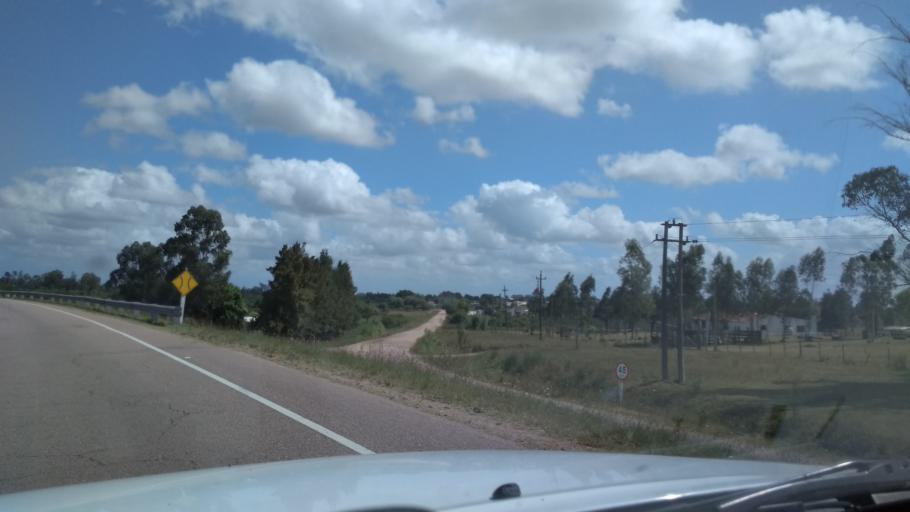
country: UY
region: Canelones
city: Sauce
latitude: -34.6384
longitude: -56.0528
